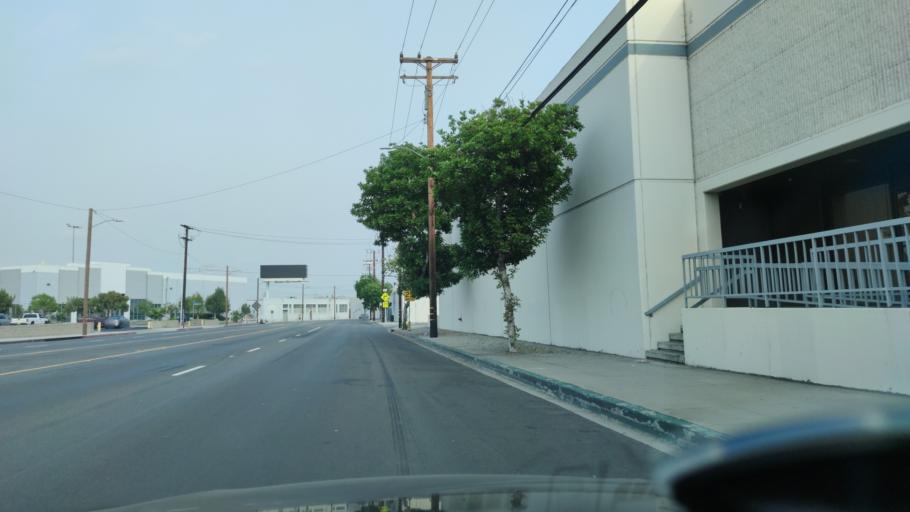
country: US
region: California
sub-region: Los Angeles County
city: Maywood
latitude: 33.9993
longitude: -118.1941
